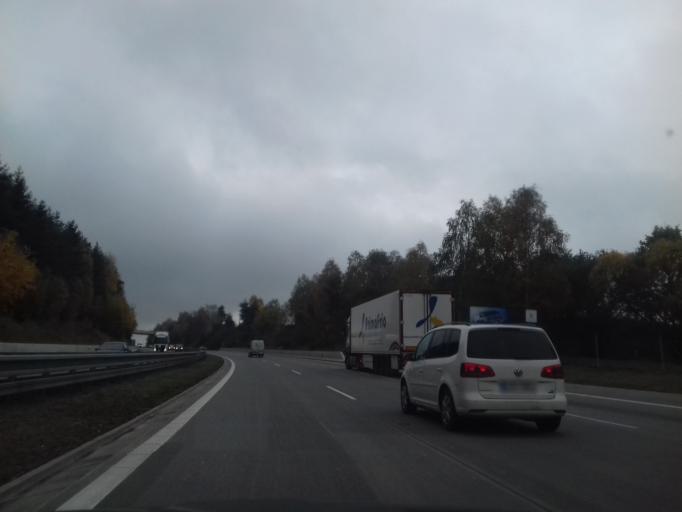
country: CZ
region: Vysocina
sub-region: Okres Pelhrimov
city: Zeliv
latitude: 49.5990
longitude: 15.1962
